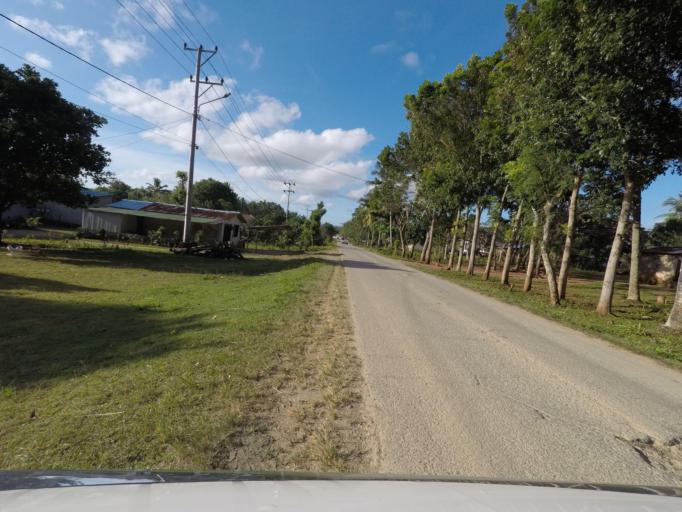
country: TL
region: Lautem
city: Lospalos
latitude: -8.4679
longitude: 126.9940
